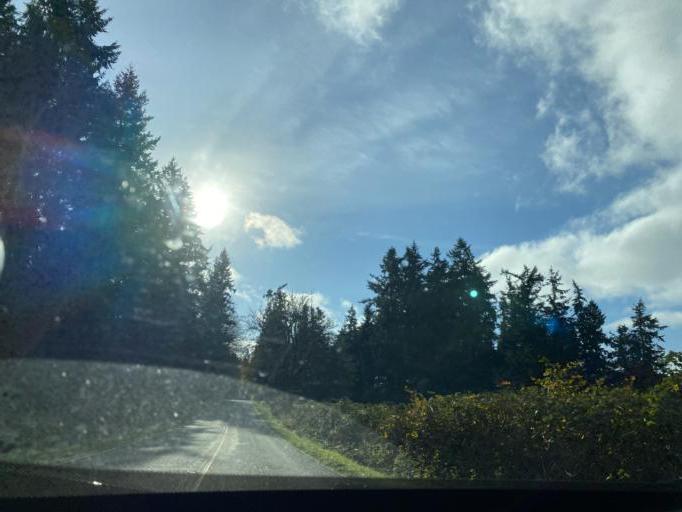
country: US
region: Washington
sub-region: Island County
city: Langley
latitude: 47.9747
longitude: -122.4514
